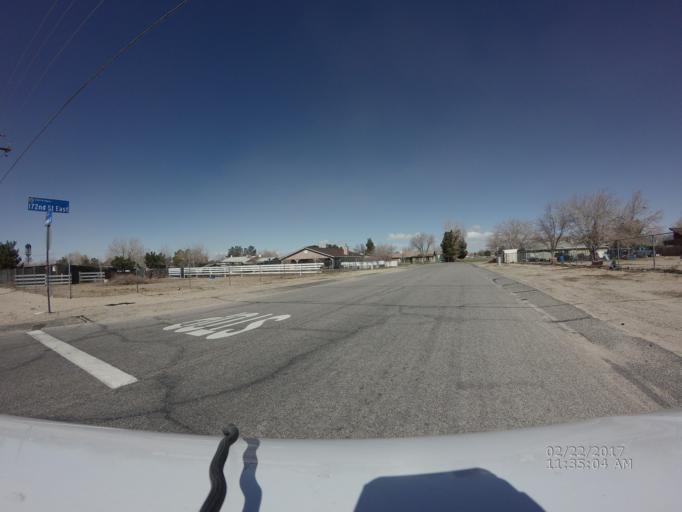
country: US
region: California
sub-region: Los Angeles County
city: Lake Los Angeles
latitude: 34.6167
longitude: -117.8224
